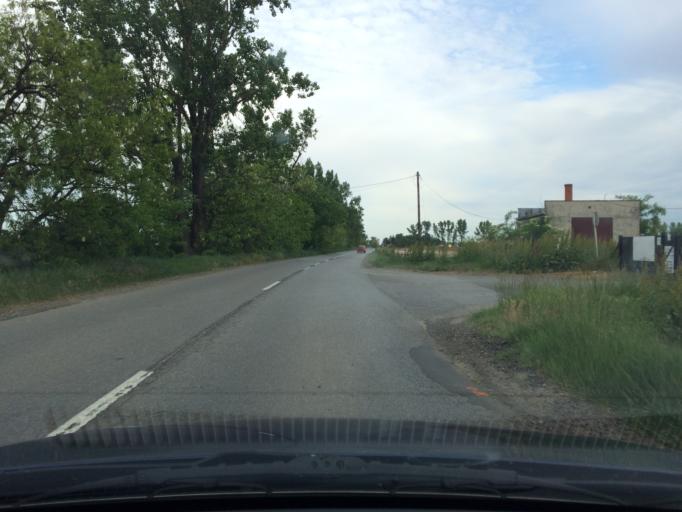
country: HU
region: Szabolcs-Szatmar-Bereg
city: Tiszavasvari
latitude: 47.9359
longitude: 21.3828
